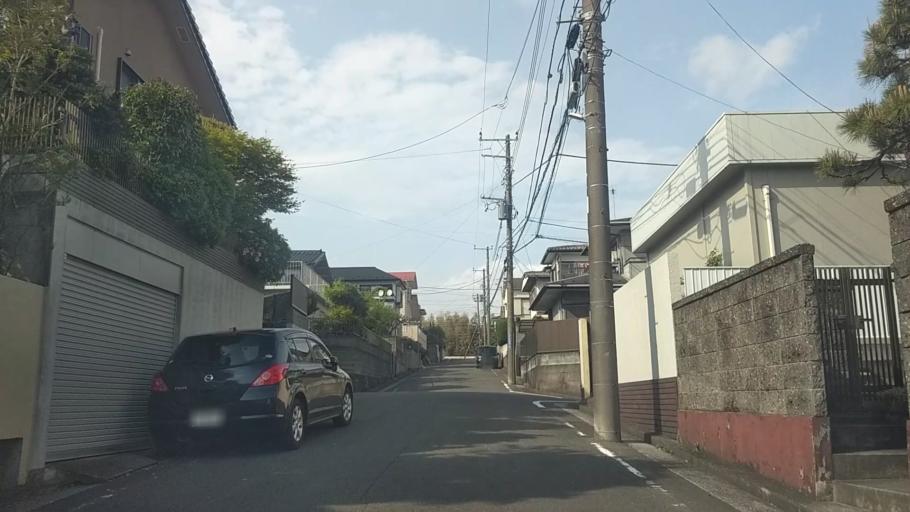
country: JP
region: Kanagawa
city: Kamakura
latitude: 35.3700
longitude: 139.5537
